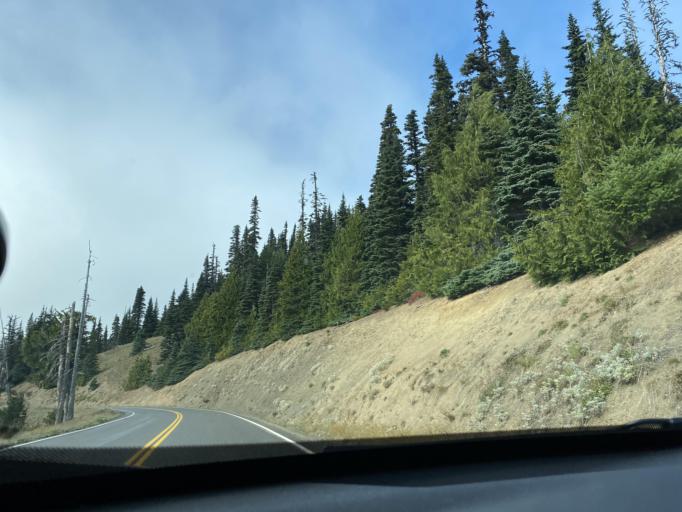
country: US
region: Washington
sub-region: Clallam County
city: Port Angeles
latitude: 47.9738
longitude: -123.4763
